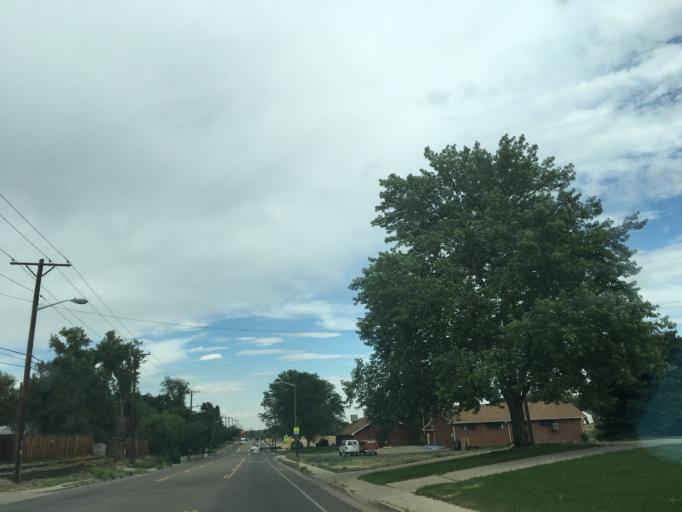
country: US
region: Colorado
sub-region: Arapahoe County
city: Sheridan
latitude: 39.6895
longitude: -105.0181
